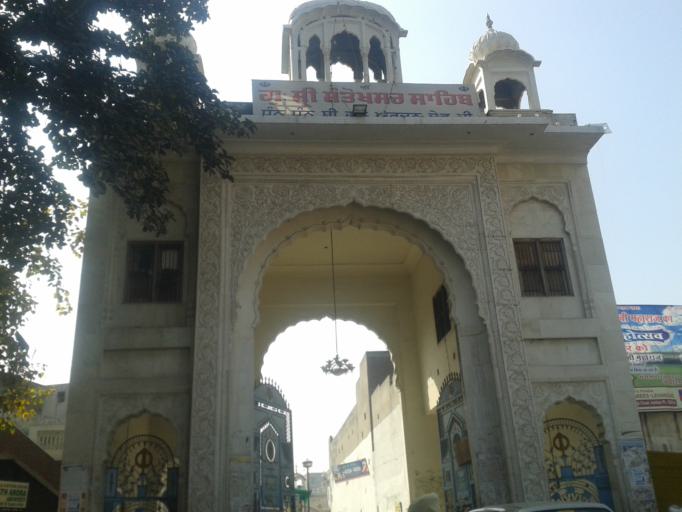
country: IN
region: Punjab
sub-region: Amritsar
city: Amritsar
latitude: 31.6255
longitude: 74.8780
